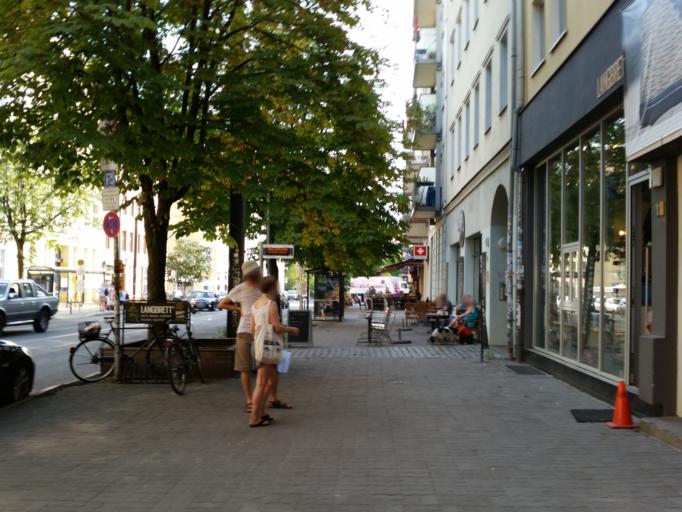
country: DE
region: Berlin
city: Berlin
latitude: 52.5348
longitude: 13.4058
